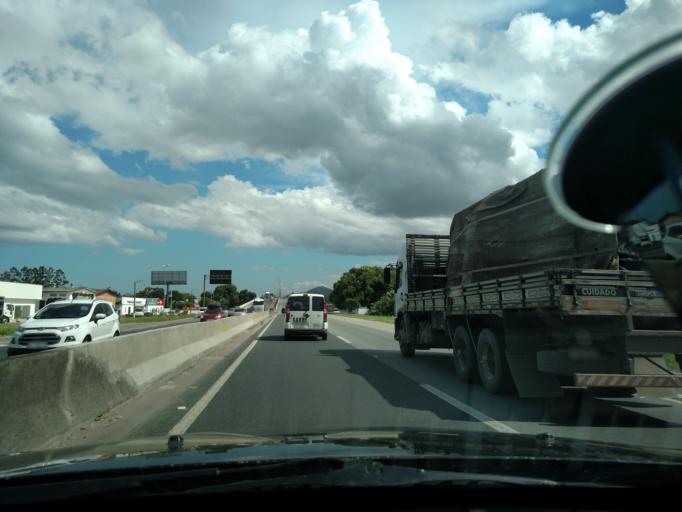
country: BR
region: Santa Catarina
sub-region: Tijucas
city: Tijucas
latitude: -27.2375
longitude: -48.6305
